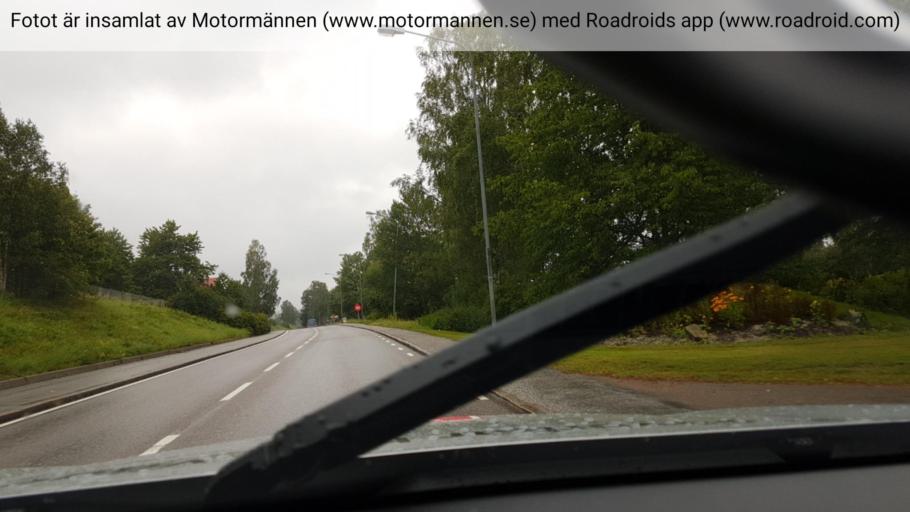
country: SE
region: Vaestra Goetaland
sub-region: Bengtsfors Kommun
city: Billingsfors
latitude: 58.9786
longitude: 12.2472
